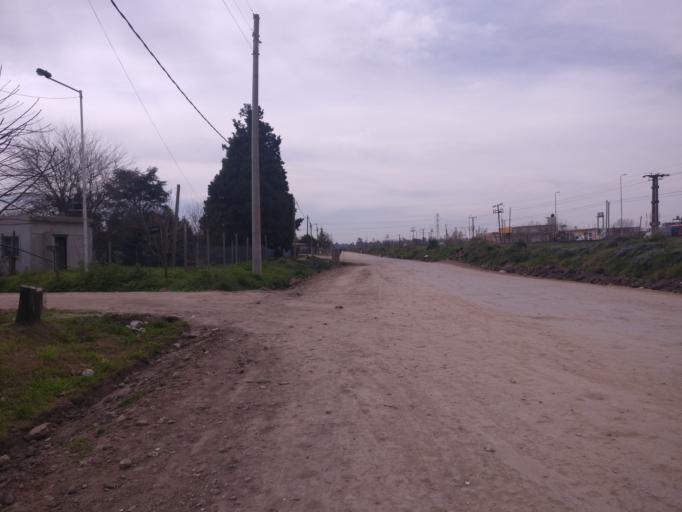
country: AR
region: Buenos Aires
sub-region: Partido de Ezeiza
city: Ezeiza
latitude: -34.9333
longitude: -58.6183
